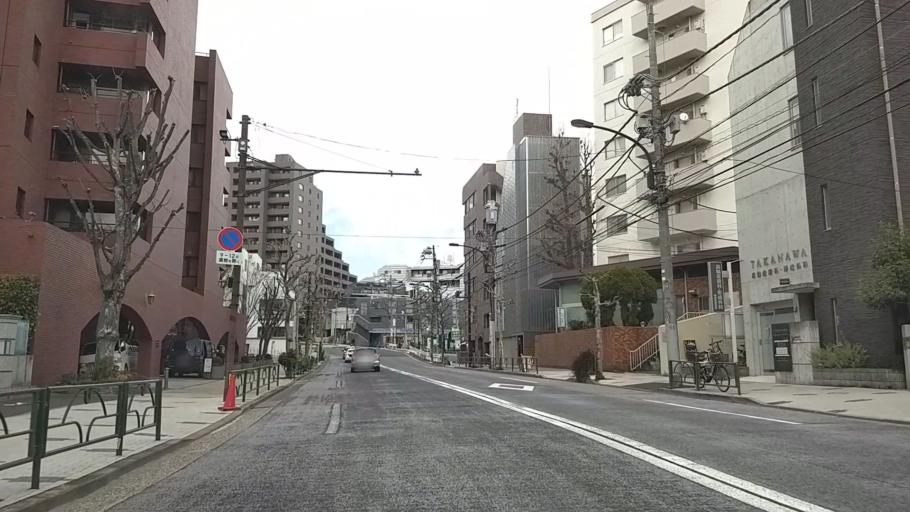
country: JP
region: Tokyo
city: Tokyo
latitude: 35.6390
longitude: 139.7385
